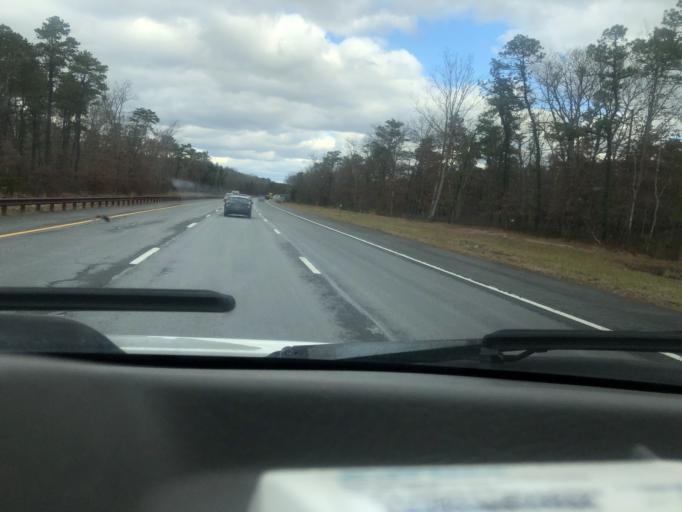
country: US
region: New Jersey
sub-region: Ocean County
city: Manahawkin
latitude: 39.6886
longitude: -74.2997
